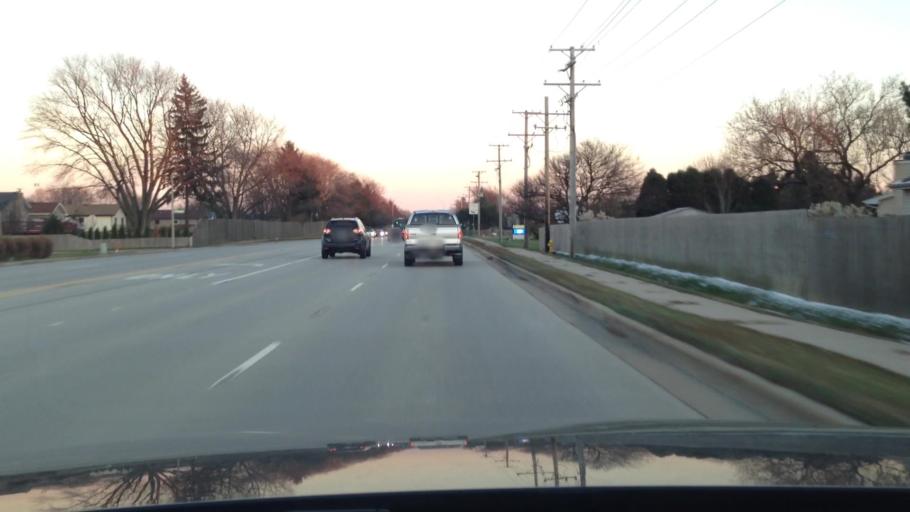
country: US
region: Illinois
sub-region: DuPage County
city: Carol Stream
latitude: 41.9416
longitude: -88.1658
